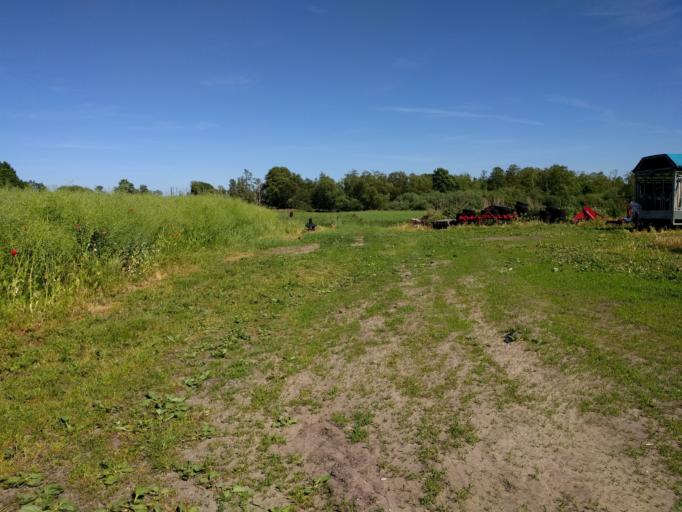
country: DK
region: South Denmark
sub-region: Kerteminde Kommune
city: Langeskov
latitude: 55.3871
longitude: 10.5814
